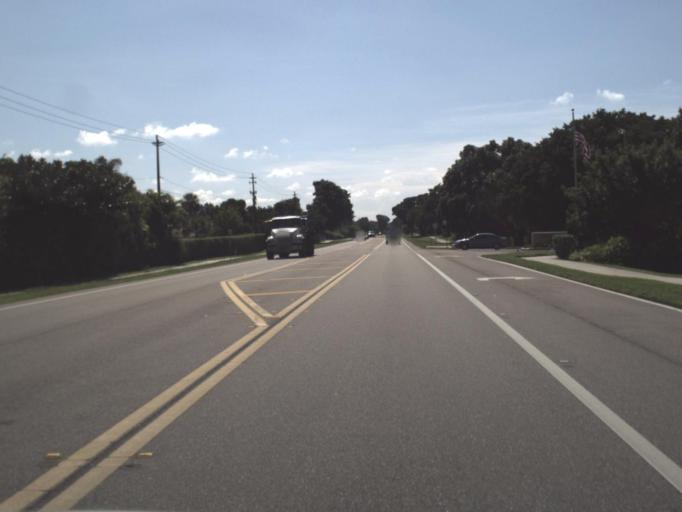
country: US
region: Florida
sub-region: Sarasota County
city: Siesta Key
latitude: 27.3501
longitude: -82.6075
